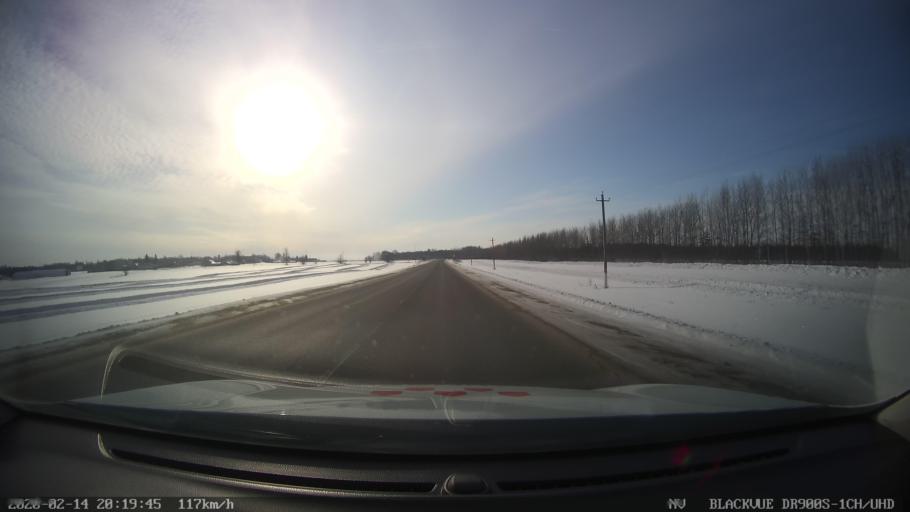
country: RU
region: Tatarstan
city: Verkhniy Uslon
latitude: 55.5660
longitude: 48.9014
